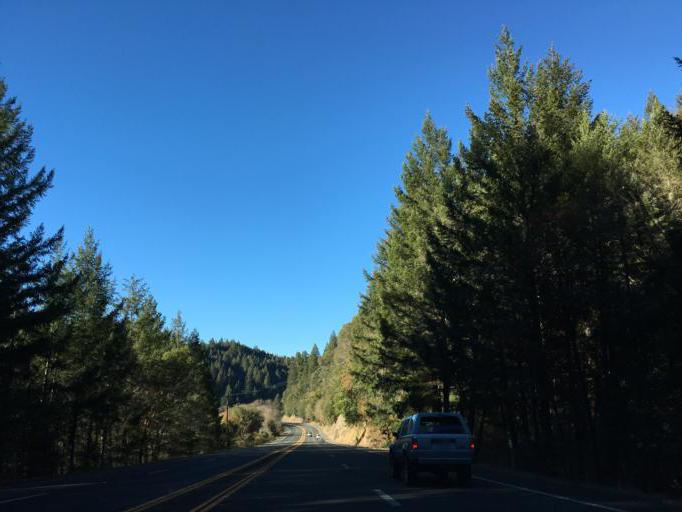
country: US
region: California
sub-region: Mendocino County
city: Brooktrails
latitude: 39.5244
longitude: -123.3989
